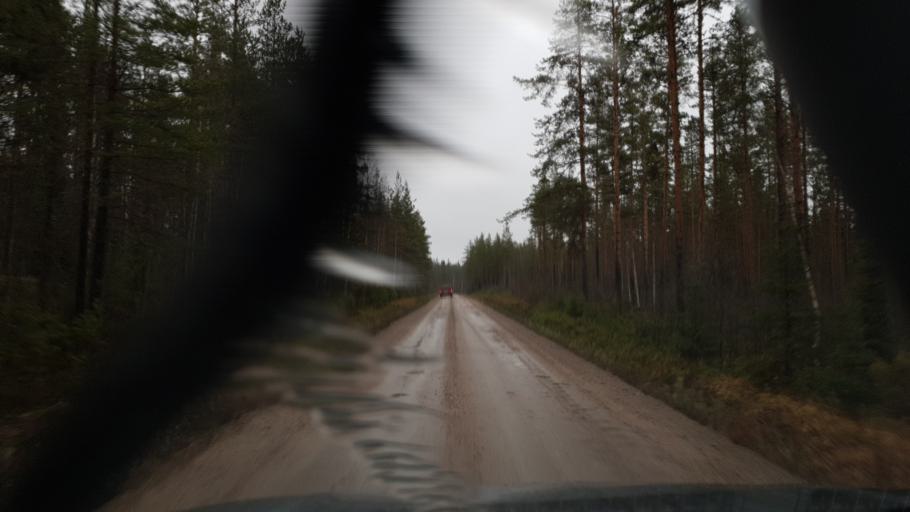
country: SE
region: Vaesternorrland
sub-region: Ange Kommun
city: Ange
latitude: 62.2155
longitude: 15.5235
